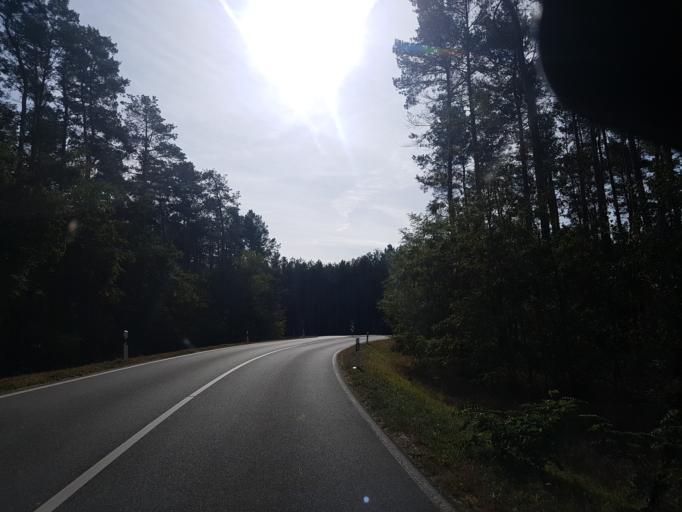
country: DE
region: Brandenburg
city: Schlieben
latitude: 51.6942
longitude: 13.4309
